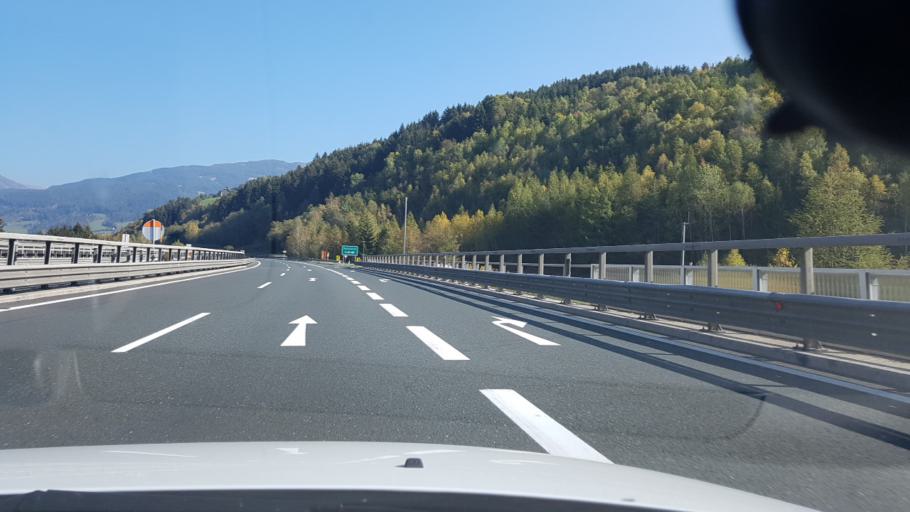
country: AT
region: Carinthia
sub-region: Politischer Bezirk Spittal an der Drau
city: Gmuend
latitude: 46.9207
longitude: 13.5788
